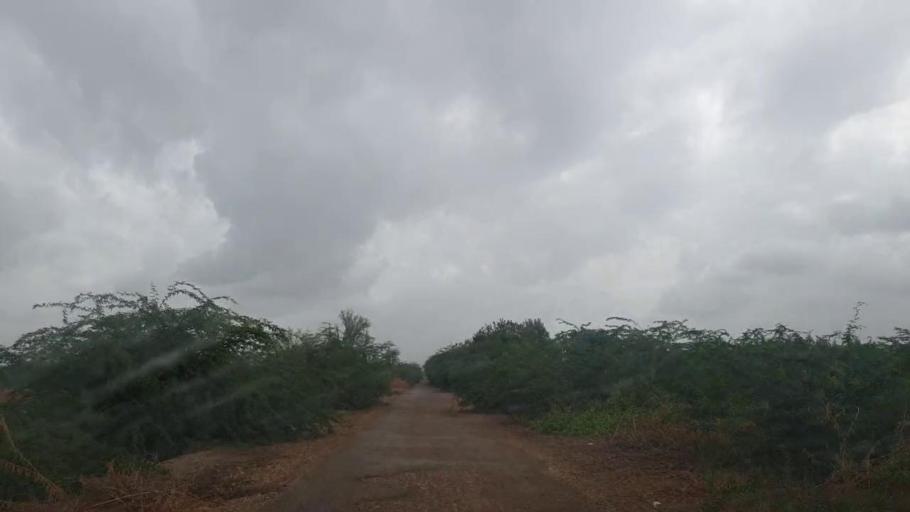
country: PK
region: Sindh
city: Naukot
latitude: 24.8701
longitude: 69.2301
